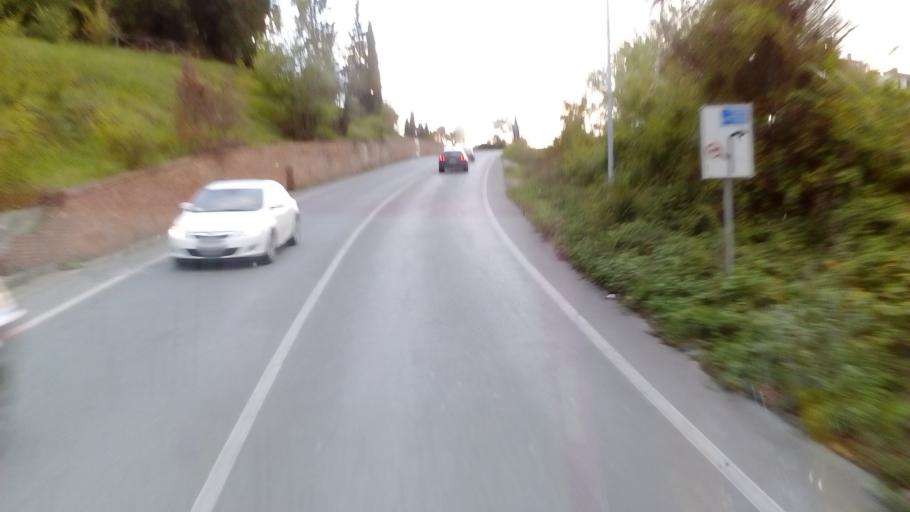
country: IT
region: Tuscany
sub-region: Province of Florence
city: Castelfiorentino
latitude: 43.6069
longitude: 10.9741
